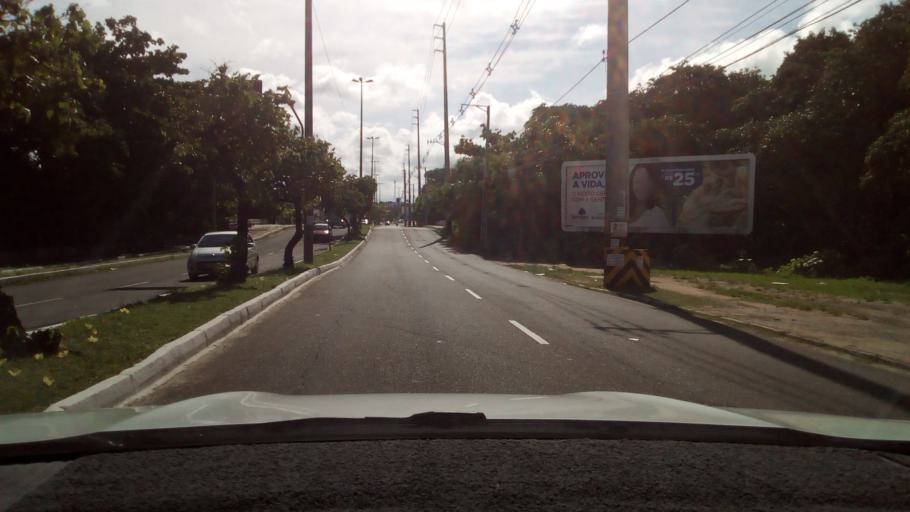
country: BR
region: Paraiba
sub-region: Joao Pessoa
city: Joao Pessoa
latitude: -7.0983
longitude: -34.8489
